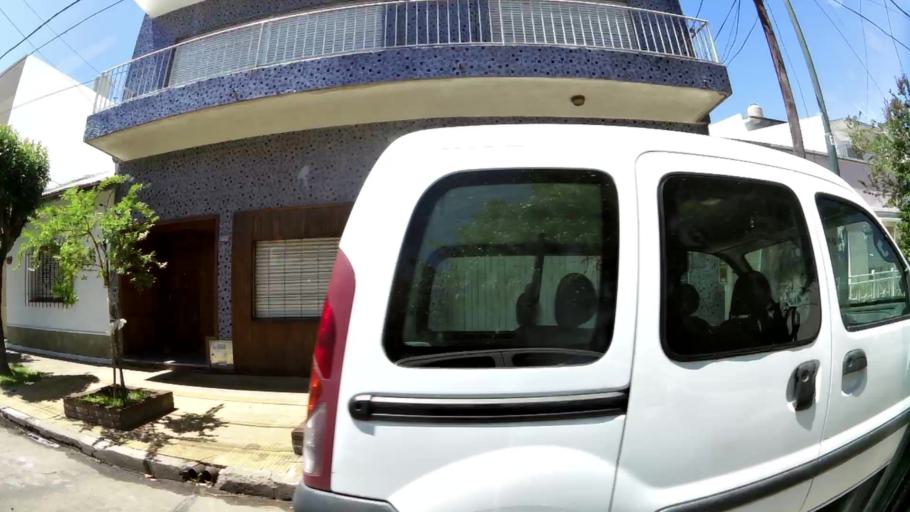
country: AR
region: Buenos Aires
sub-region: Partido de San Isidro
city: San Isidro
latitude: -34.5026
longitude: -58.5322
